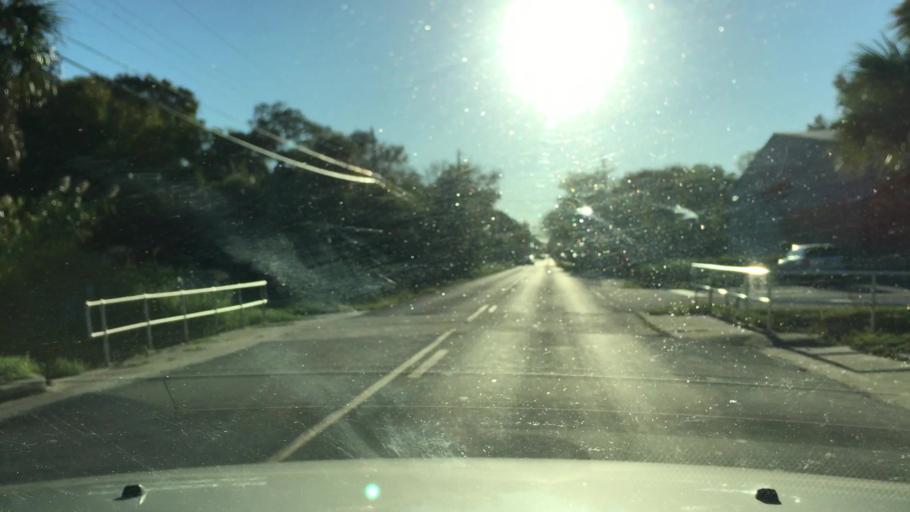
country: US
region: Florida
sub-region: Volusia County
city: Holly Hill
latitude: 29.2298
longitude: -81.0377
